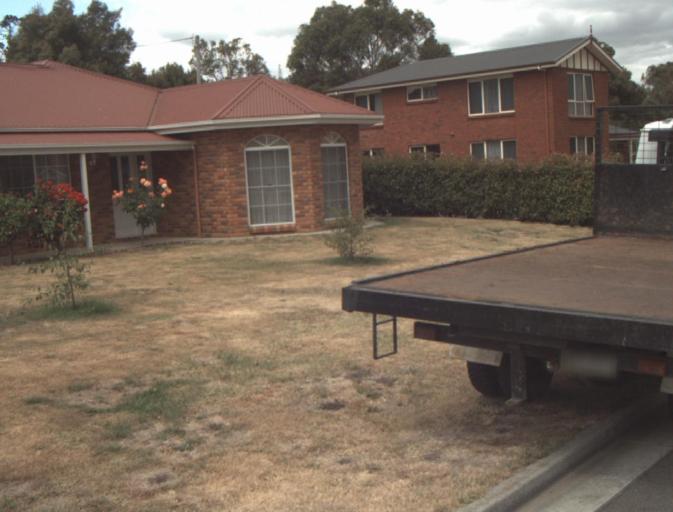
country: AU
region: Tasmania
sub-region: Launceston
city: Newstead
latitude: -41.4496
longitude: 147.1908
